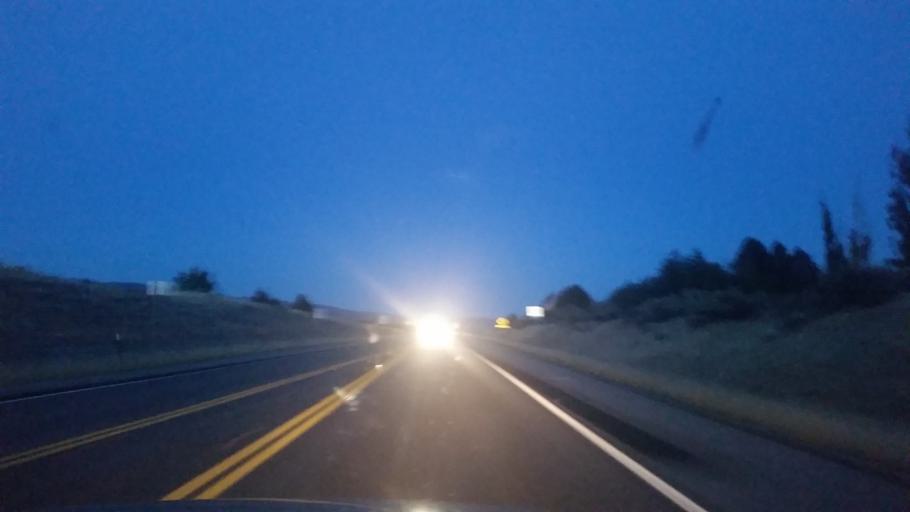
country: US
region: Washington
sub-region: Chelan County
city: South Wenatchee
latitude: 47.3831
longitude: -120.2382
